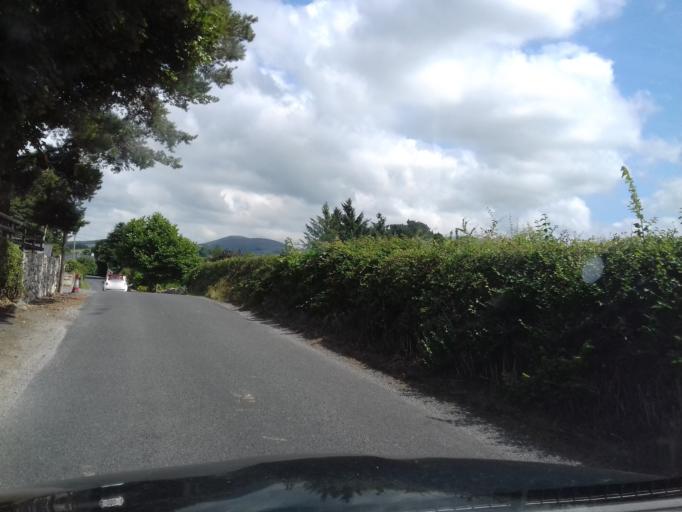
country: IE
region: Leinster
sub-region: Kilkenny
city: Graiguenamanagh
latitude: 52.6037
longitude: -6.9064
